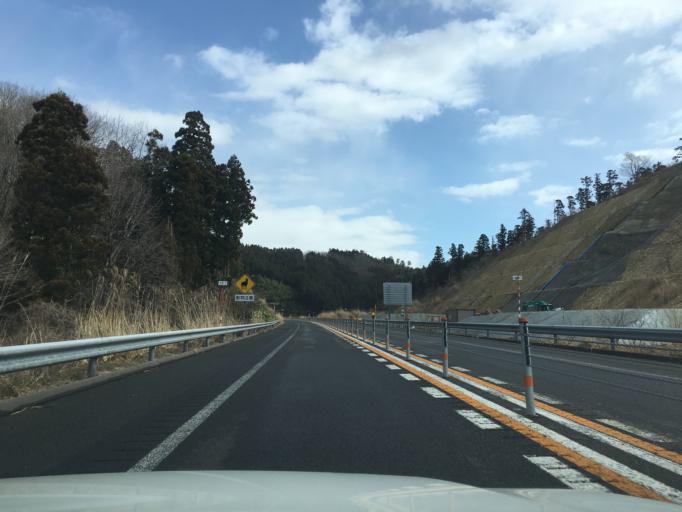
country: JP
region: Akita
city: Akita Shi
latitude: 39.5547
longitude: 140.0806
